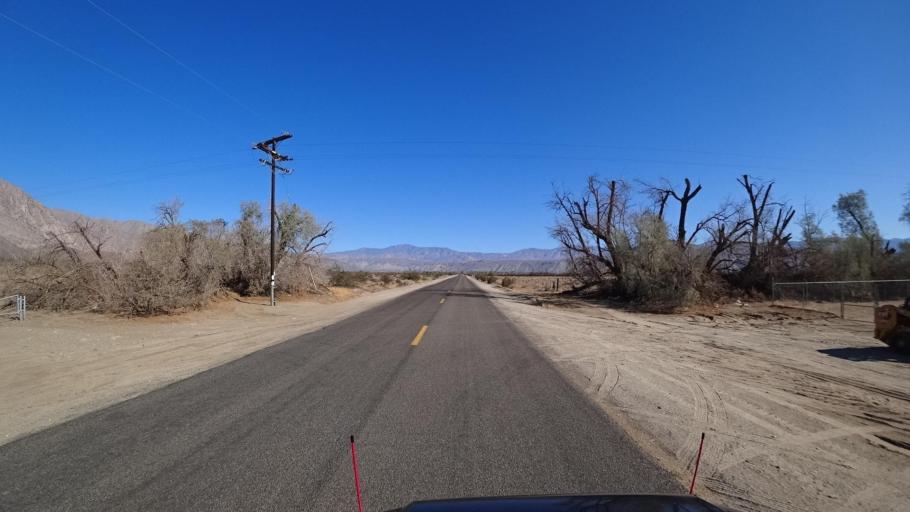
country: US
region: California
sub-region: San Diego County
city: Borrego Springs
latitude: 33.2769
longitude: -116.3751
